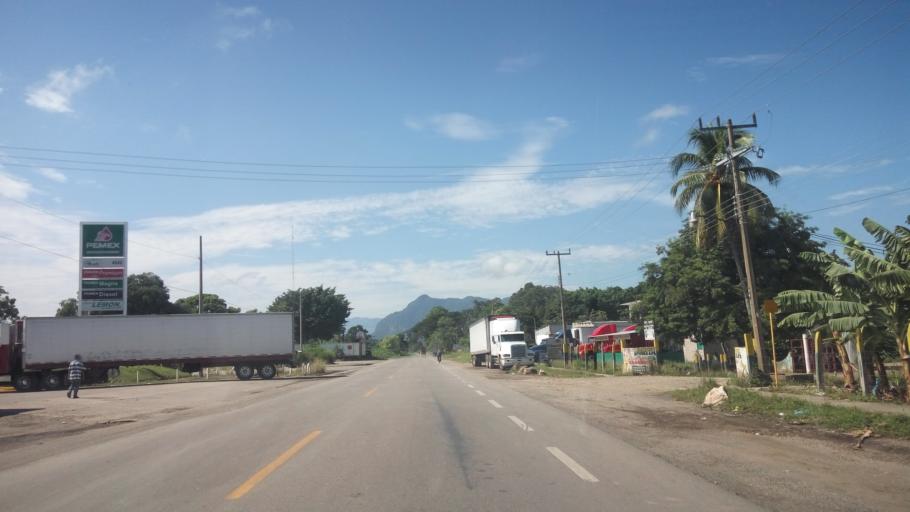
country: MX
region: Tabasco
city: Teapa
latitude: 17.5920
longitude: -92.9653
